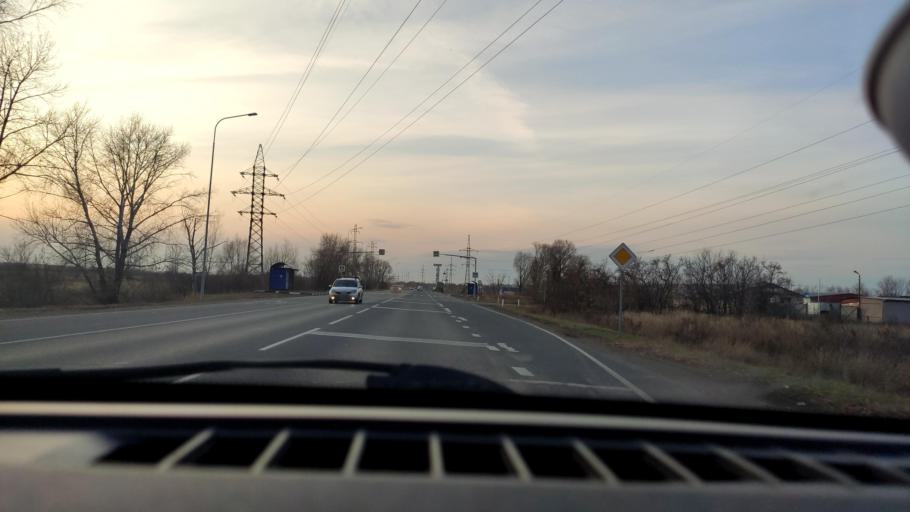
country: RU
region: Samara
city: Samara
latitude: 53.1297
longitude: 50.1533
